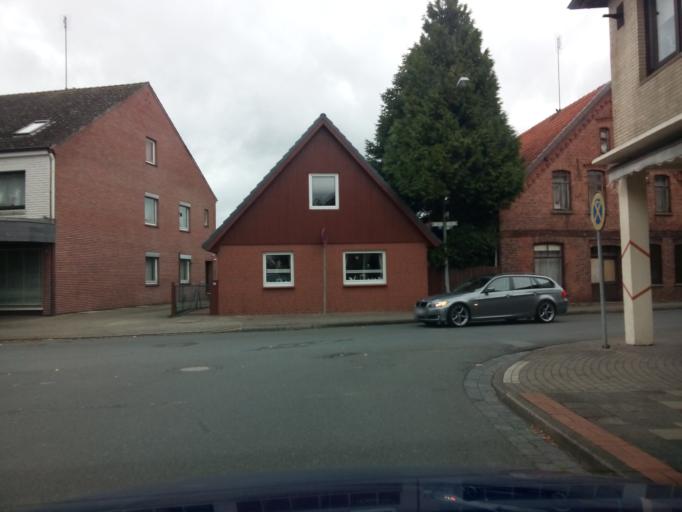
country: DE
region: Lower Saxony
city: Beverstedt
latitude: 53.4354
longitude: 8.8219
